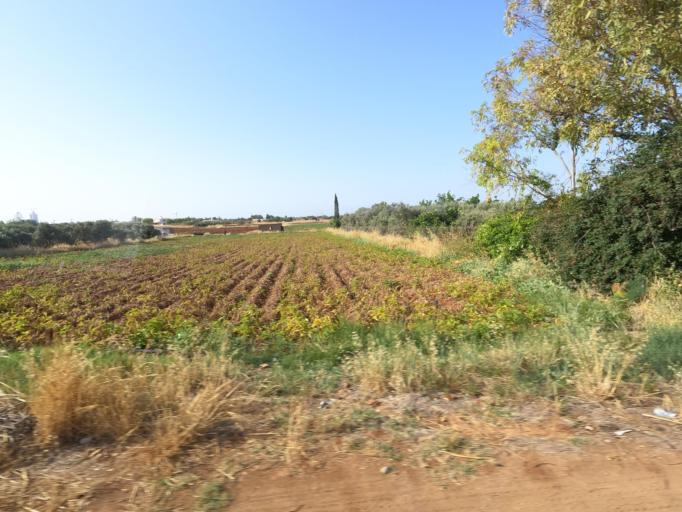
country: CY
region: Ammochostos
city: Liopetri
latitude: 35.0010
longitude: 33.9207
